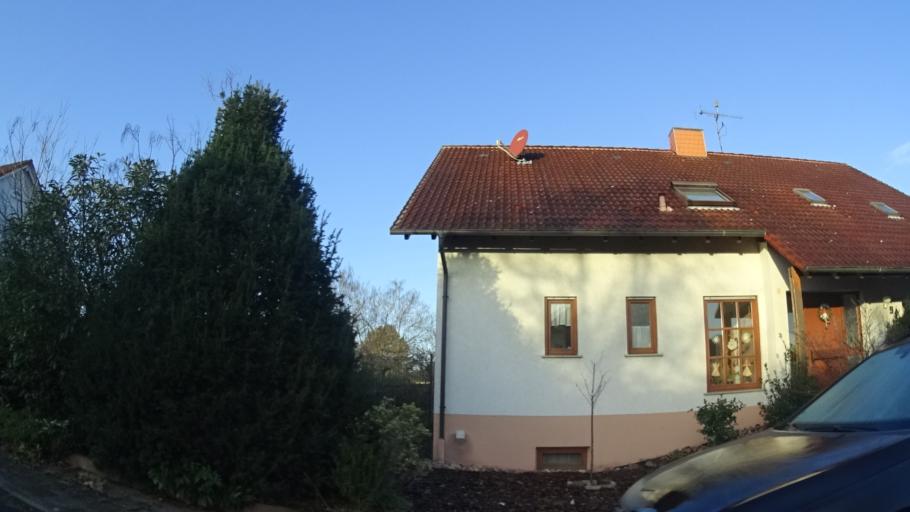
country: DE
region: Baden-Wuerttemberg
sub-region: Karlsruhe Region
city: Forst
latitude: 49.1574
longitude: 8.5810
